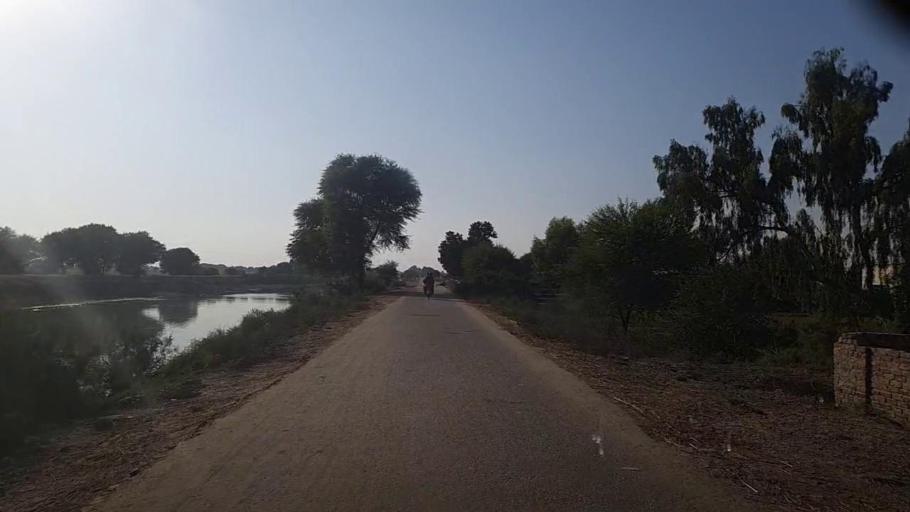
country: PK
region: Sindh
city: Tangwani
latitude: 28.3014
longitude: 68.9325
